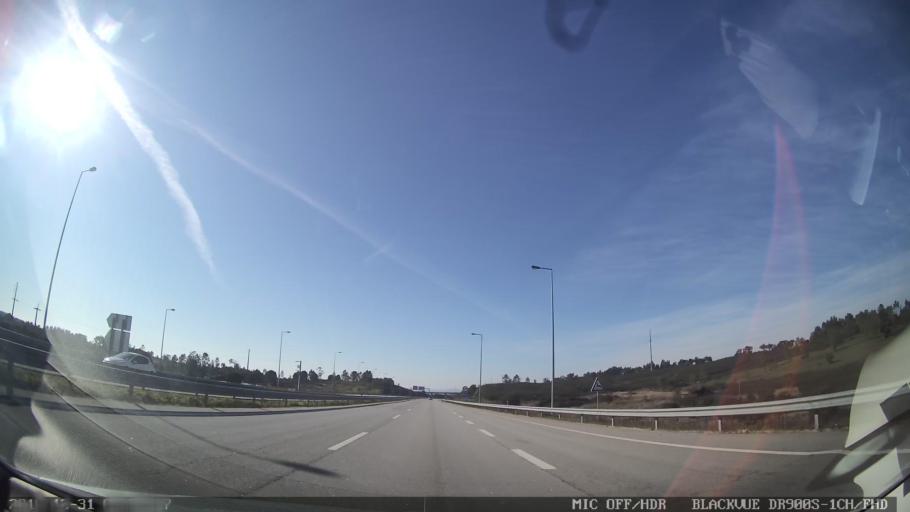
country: PT
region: Castelo Branco
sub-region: Castelo Branco
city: Castelo Branco
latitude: 39.7599
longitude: -7.6080
